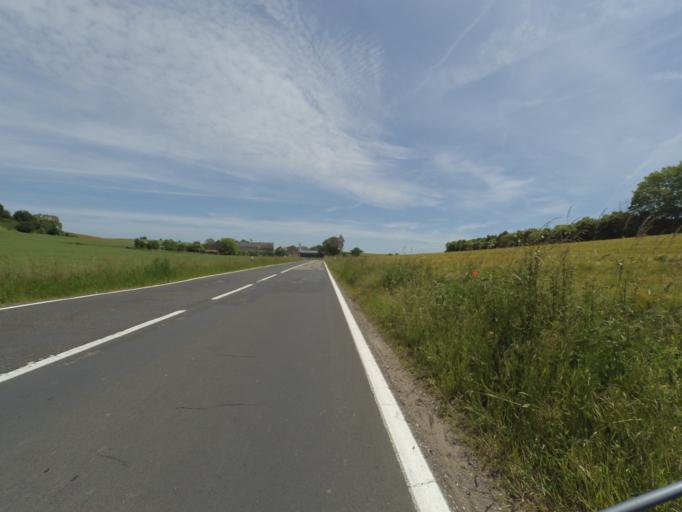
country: DE
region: Rheinland-Pfalz
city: Kerben
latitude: 50.3135
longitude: 7.3708
